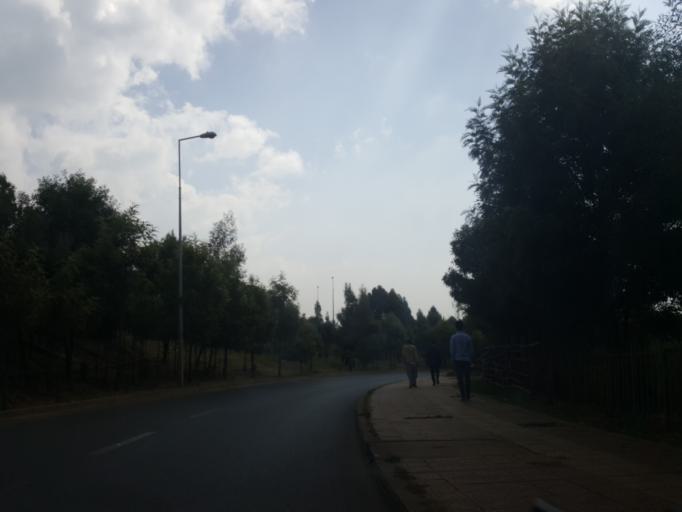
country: ET
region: Adis Abeba
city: Addis Ababa
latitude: 9.0695
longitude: 38.7201
